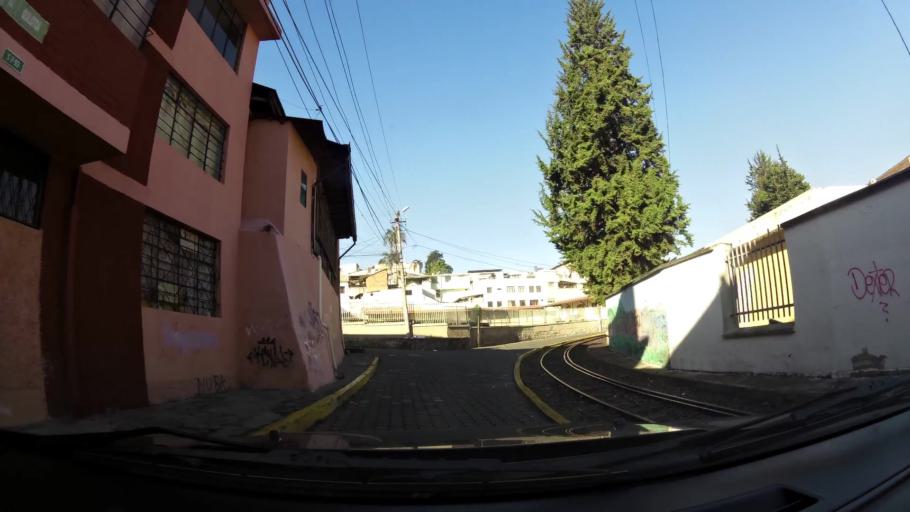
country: EC
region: Pichincha
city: Quito
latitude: -0.2390
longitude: -78.5151
